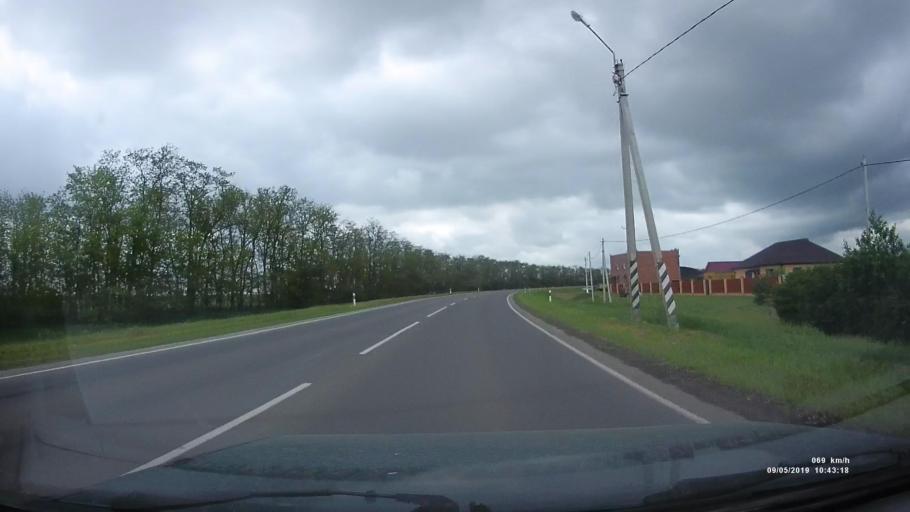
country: RU
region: Rostov
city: Peshkovo
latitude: 47.0098
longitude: 39.4039
